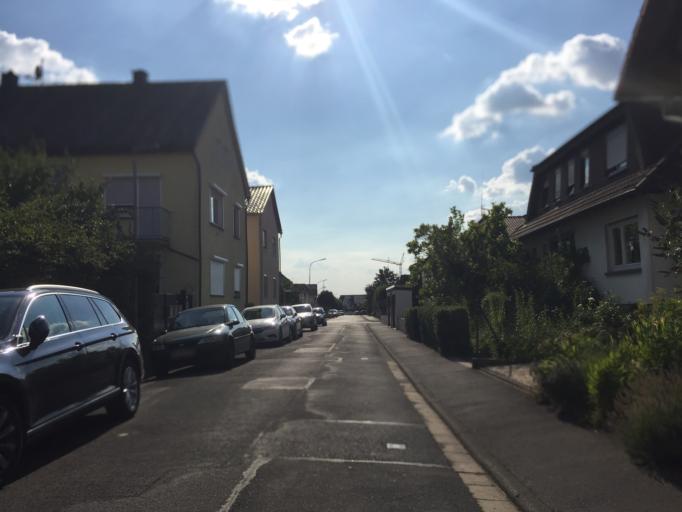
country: DE
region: Hesse
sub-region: Regierungsbezirk Giessen
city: Langgons
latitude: 50.5322
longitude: 8.7073
